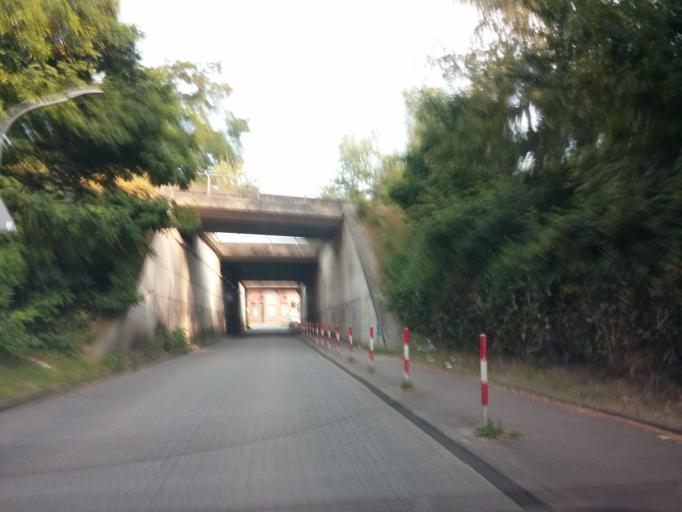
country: DE
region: North Rhine-Westphalia
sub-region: Regierungsbezirk Munster
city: Bottrop
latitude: 51.5187
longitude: 6.9520
